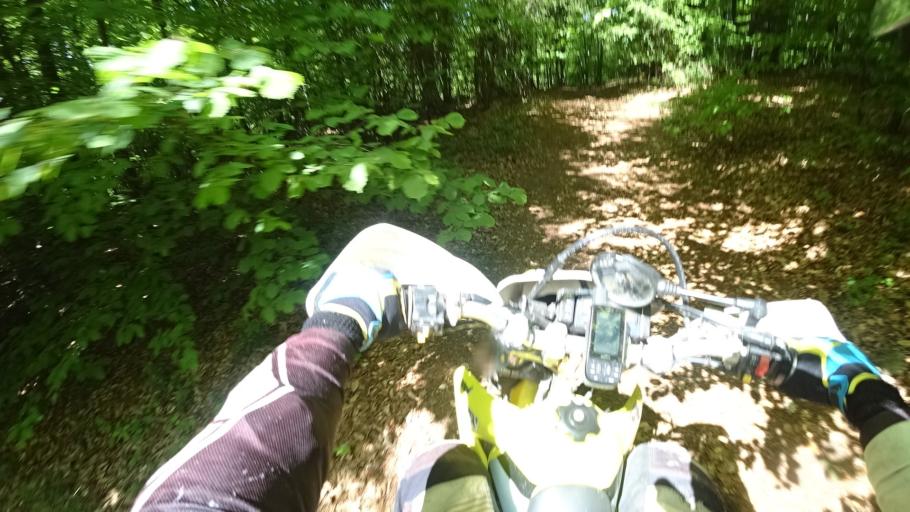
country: HR
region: Zagrebacka
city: Jablanovec
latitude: 45.8515
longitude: 15.8655
